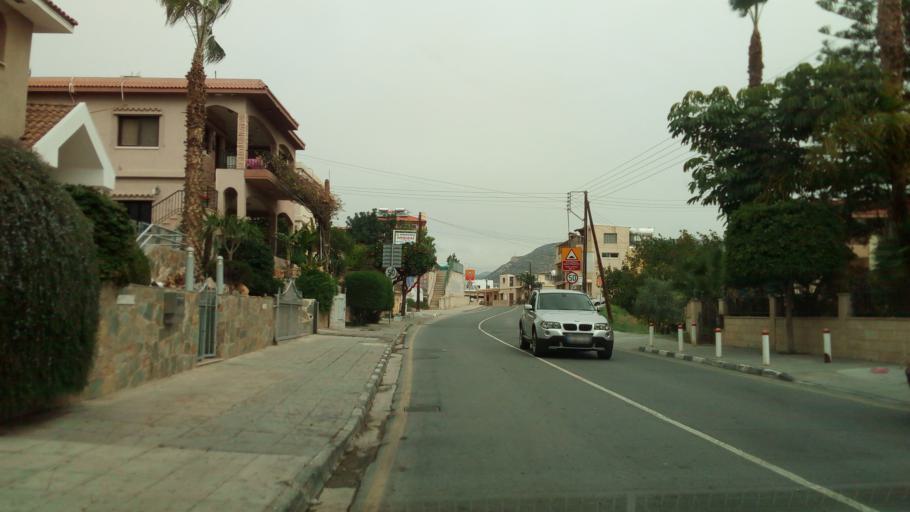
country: CY
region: Limassol
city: Mouttagiaka
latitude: 34.7157
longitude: 33.0861
